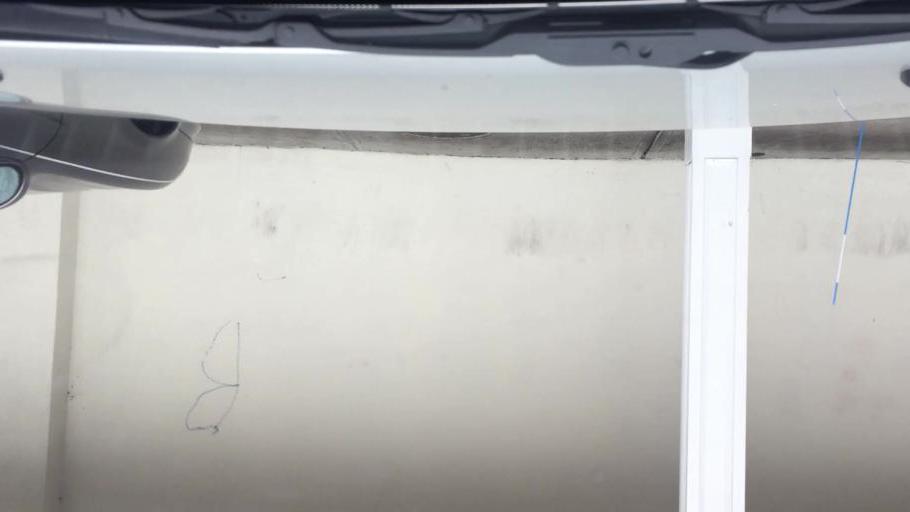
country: US
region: New Jersey
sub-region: Middlesex County
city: East Brunswick
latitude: 40.4183
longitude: -74.4113
